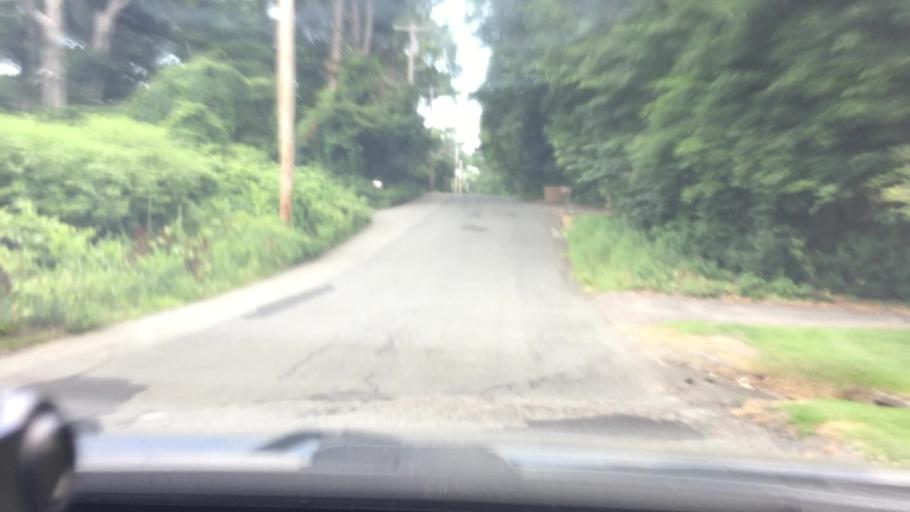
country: US
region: New York
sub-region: Suffolk County
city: Mount Sinai
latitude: 40.9240
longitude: -73.0147
